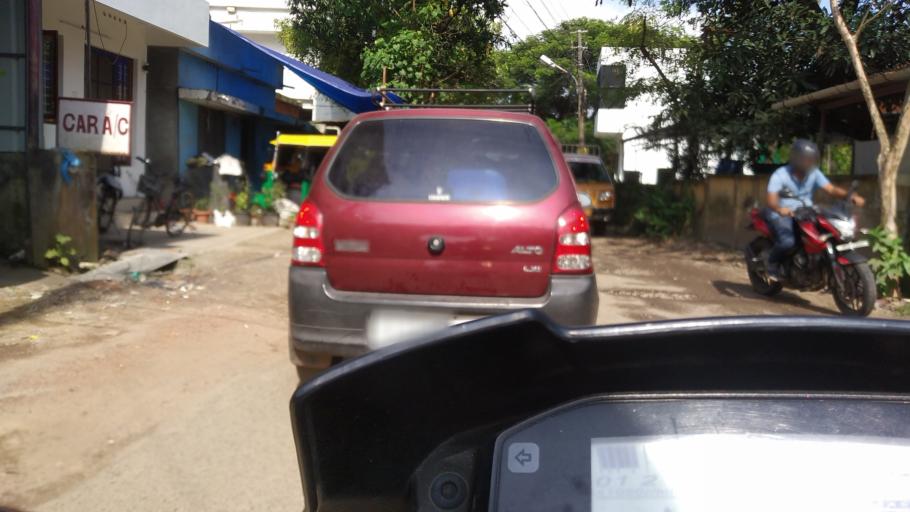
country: IN
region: Kerala
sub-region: Ernakulam
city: Cochin
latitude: 9.9811
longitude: 76.2965
